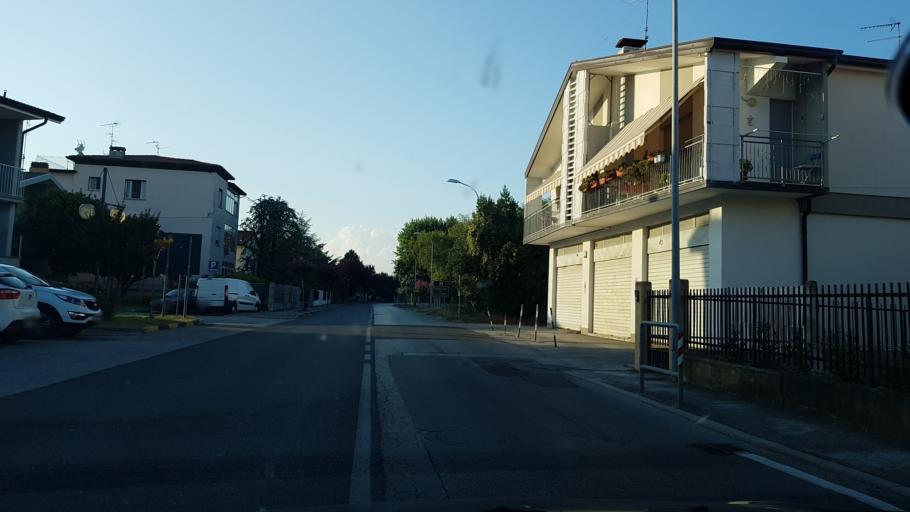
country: IT
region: Friuli Venezia Giulia
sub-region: Provincia di Gorizia
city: Staranzano
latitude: 45.8063
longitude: 13.5054
